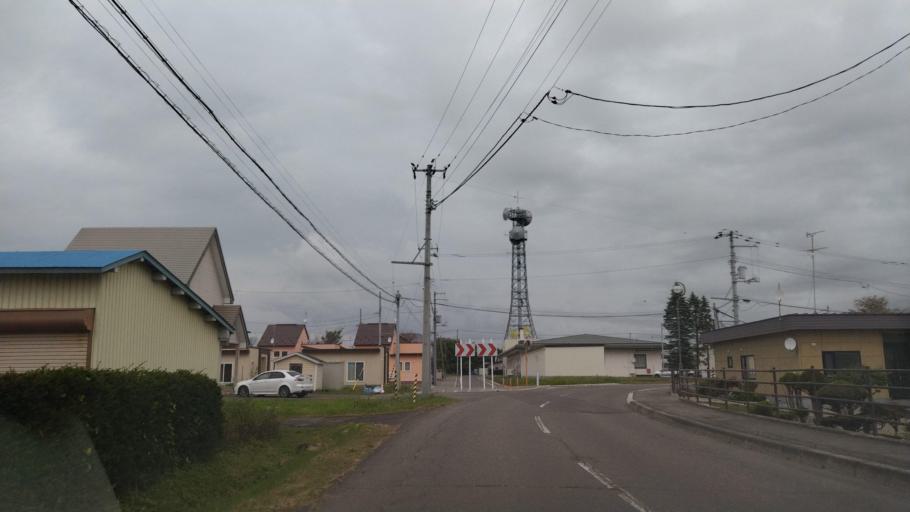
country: JP
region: Hokkaido
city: Otofuke
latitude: 43.2242
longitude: 143.2862
